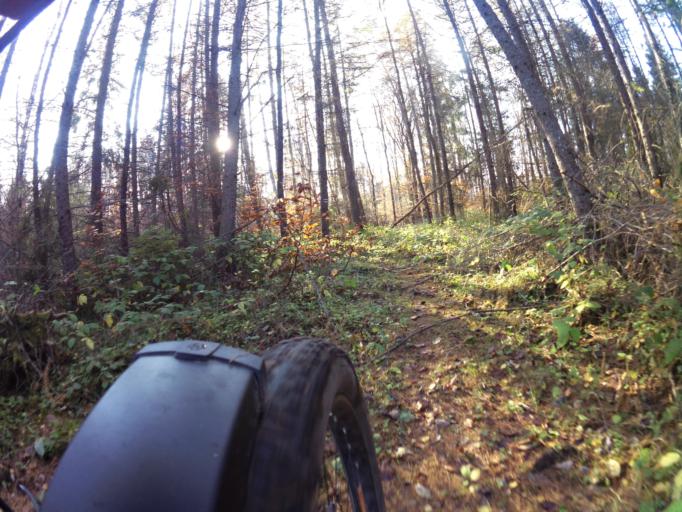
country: PL
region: Pomeranian Voivodeship
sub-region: Powiat pucki
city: Krokowa
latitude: 54.7277
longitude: 18.2117
